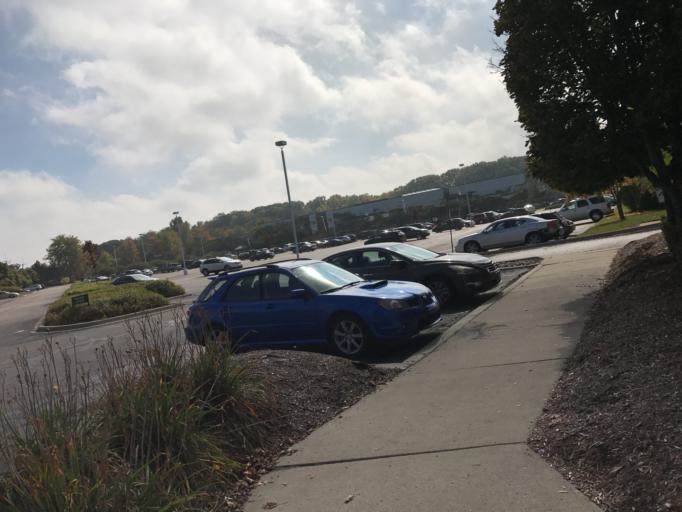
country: US
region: Michigan
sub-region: Oakland County
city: Franklin
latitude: 42.5240
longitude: -83.3501
